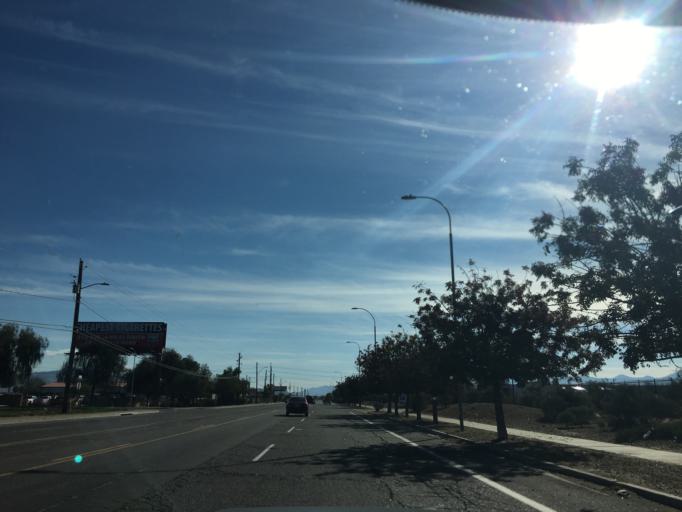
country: US
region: Arizona
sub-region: Maricopa County
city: Laveen
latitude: 33.4211
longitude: -112.1696
